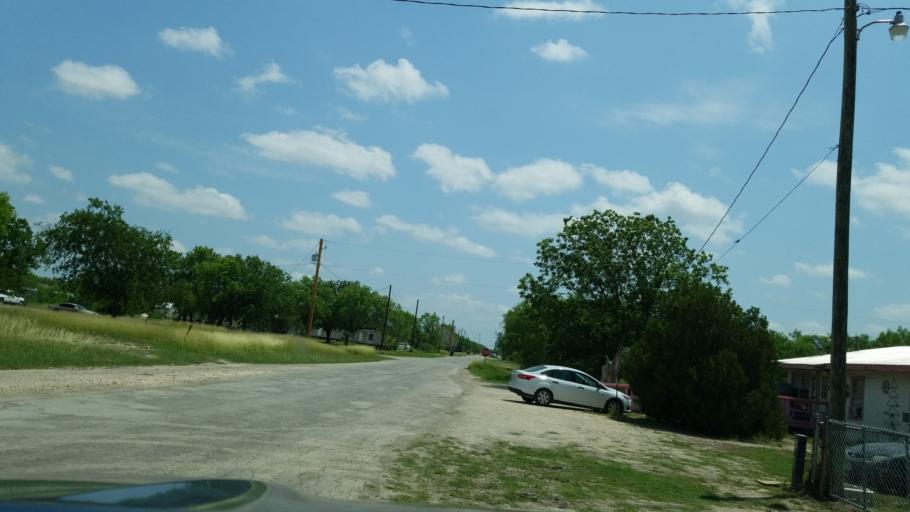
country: US
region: Texas
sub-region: Zavala County
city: La Pryor
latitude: 28.9403
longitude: -99.8414
